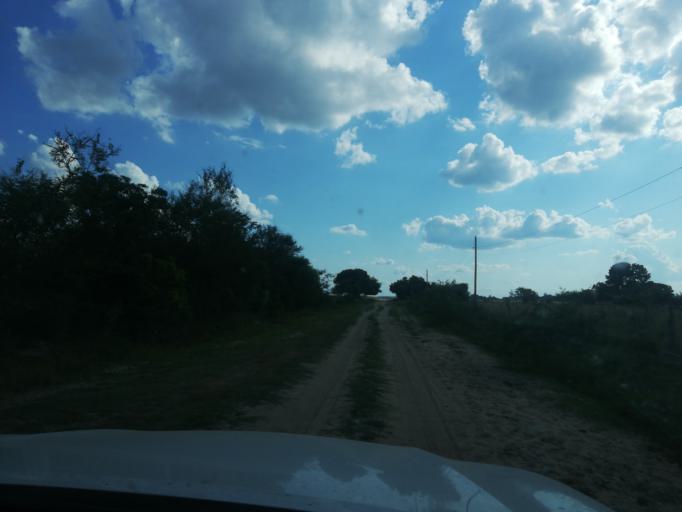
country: AR
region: Corrientes
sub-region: Departamento de San Miguel
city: San Miguel
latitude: -27.9909
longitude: -57.5698
